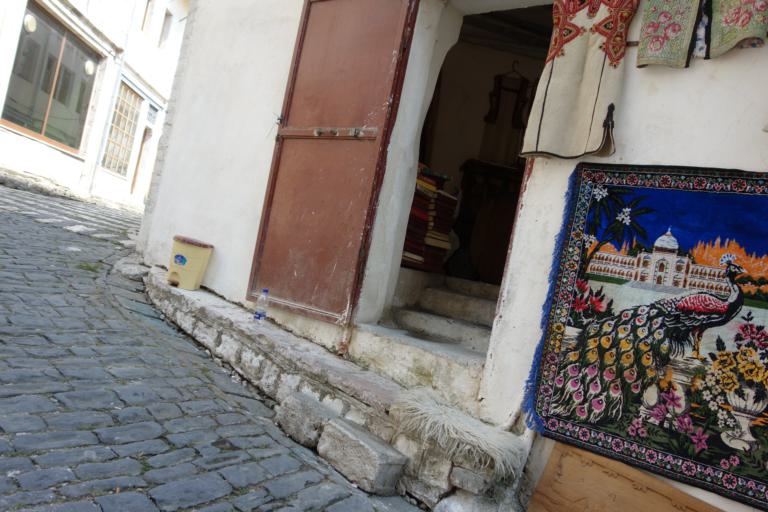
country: AL
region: Gjirokaster
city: Gjirokaster
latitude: 40.0743
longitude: 20.1384
